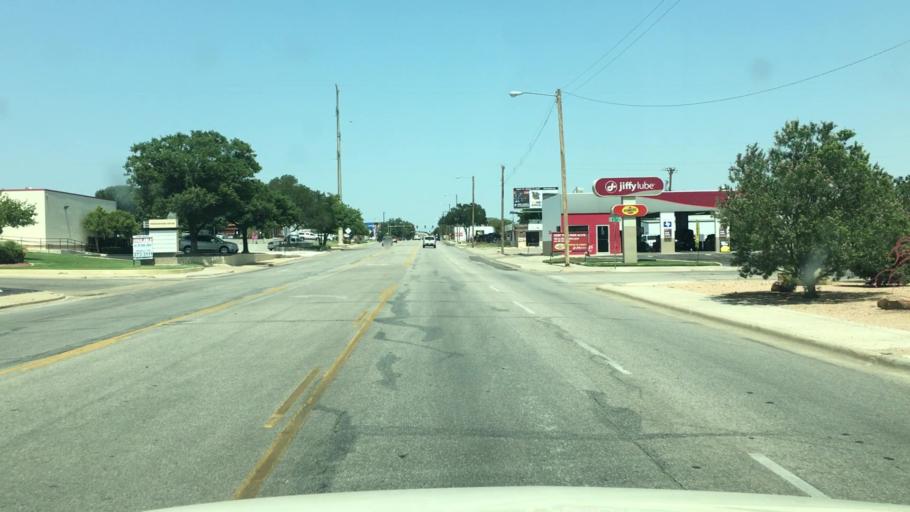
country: US
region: Texas
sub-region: Potter County
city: Amarillo
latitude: 35.1972
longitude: -101.8167
